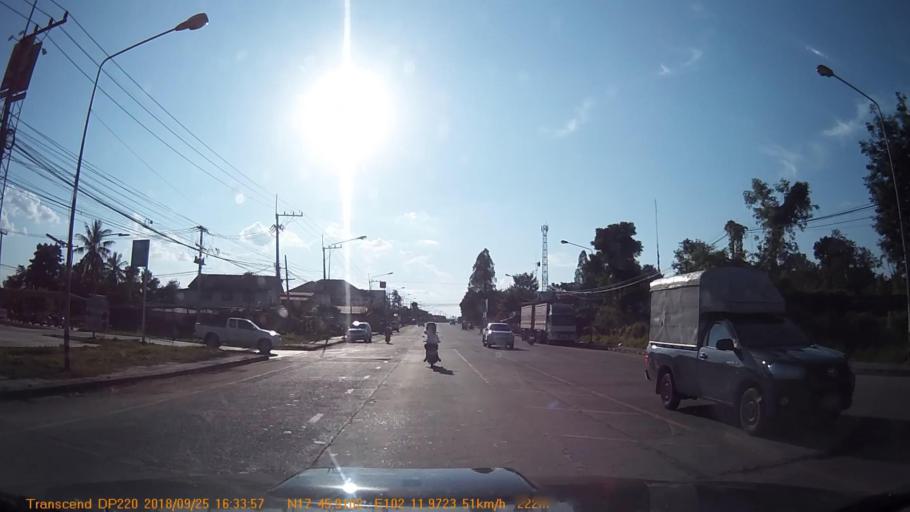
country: TH
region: Changwat Udon Thani
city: Nam Som
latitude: 17.7652
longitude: 102.1994
